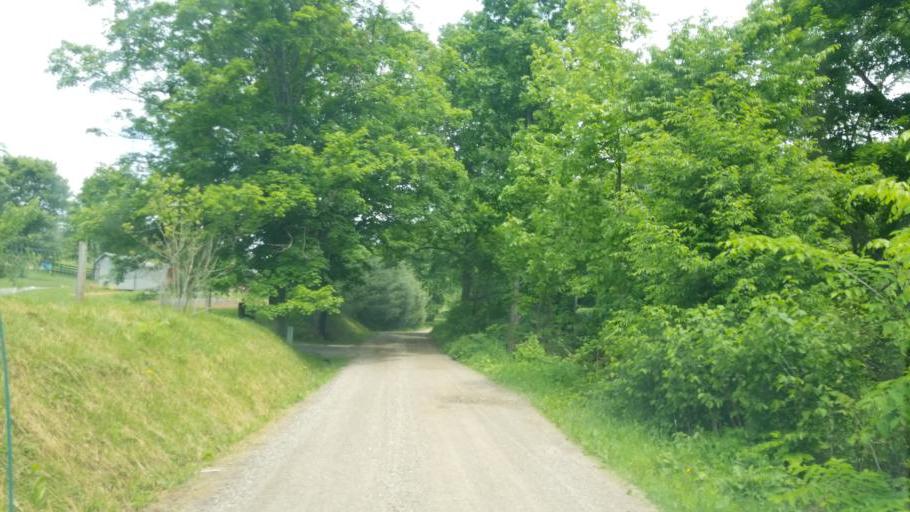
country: US
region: Ohio
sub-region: Coshocton County
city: West Lafayette
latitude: 40.4058
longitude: -81.7956
